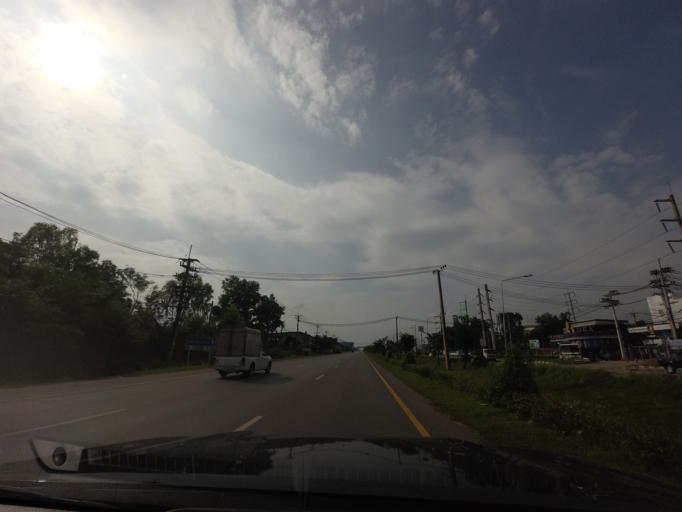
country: TH
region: Nong Khai
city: Nong Khai
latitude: 17.8205
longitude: 102.7576
